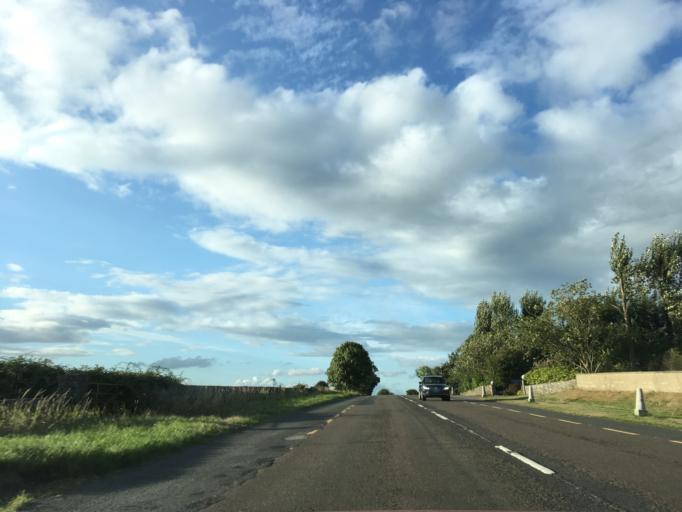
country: IE
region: Munster
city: Cashel
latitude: 52.4899
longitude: -7.8905
